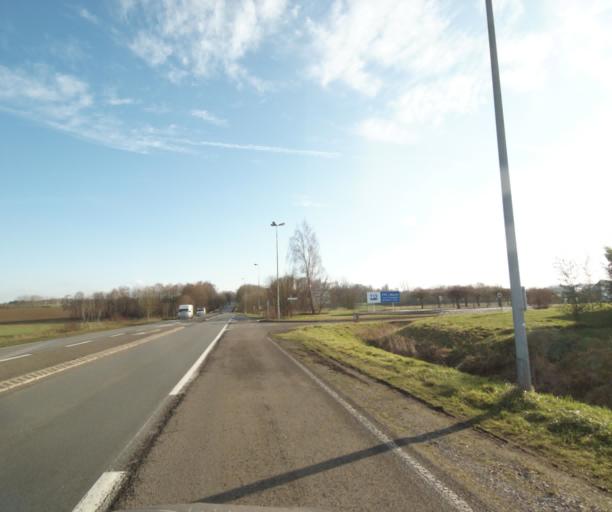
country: FR
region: Nord-Pas-de-Calais
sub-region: Departement du Nord
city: Marly
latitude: 50.3523
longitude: 3.5661
